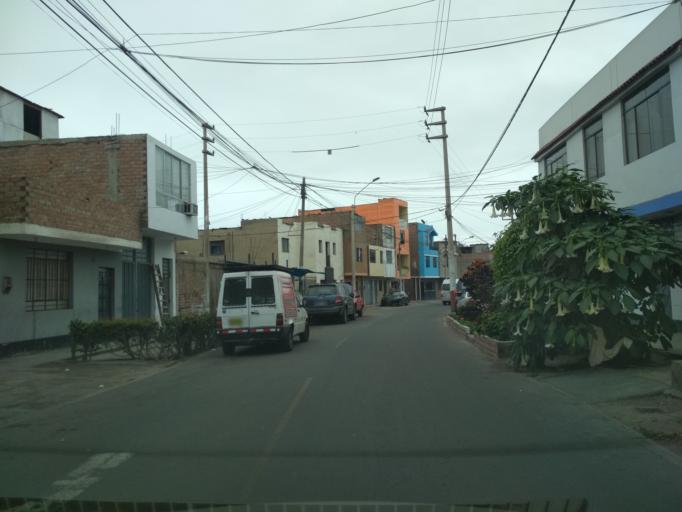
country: PE
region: Callao
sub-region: Callao
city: Callao
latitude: -12.0528
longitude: -77.1012
